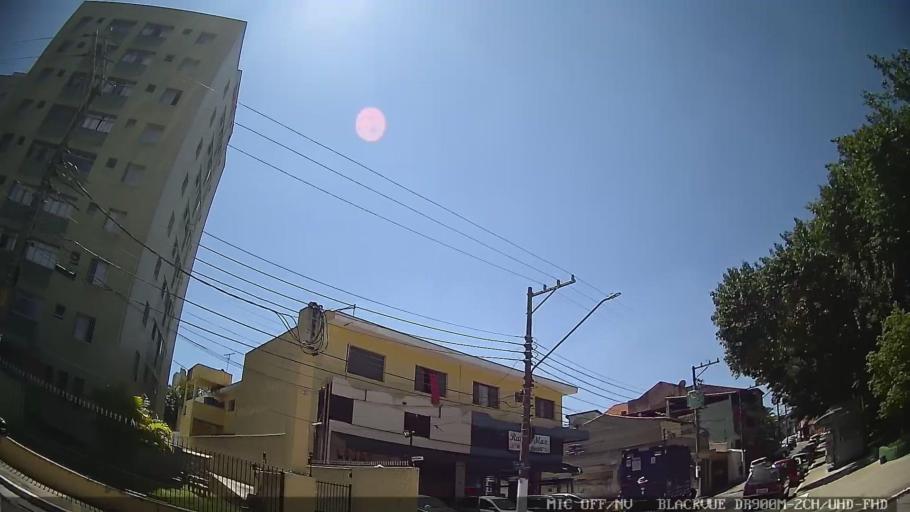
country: BR
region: Sao Paulo
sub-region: Sao Caetano Do Sul
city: Sao Caetano do Sul
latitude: -23.5907
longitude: -46.5388
